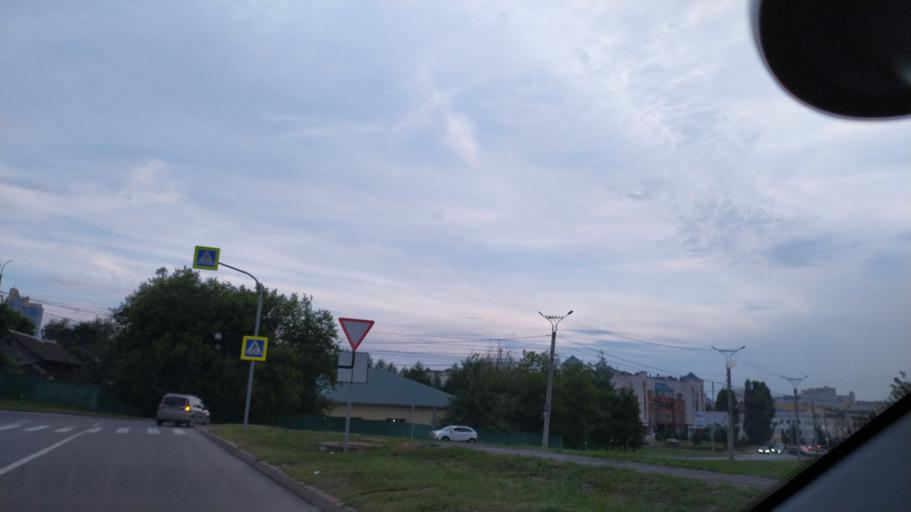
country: RU
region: Chuvashia
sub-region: Cheboksarskiy Rayon
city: Cheboksary
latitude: 56.1458
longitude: 47.2586
